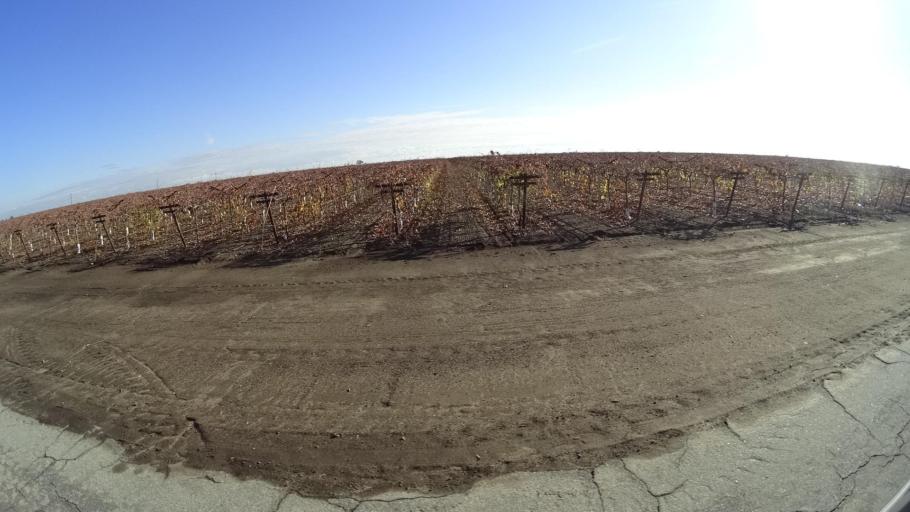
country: US
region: California
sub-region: Kern County
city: Delano
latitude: 35.7157
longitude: -119.2942
